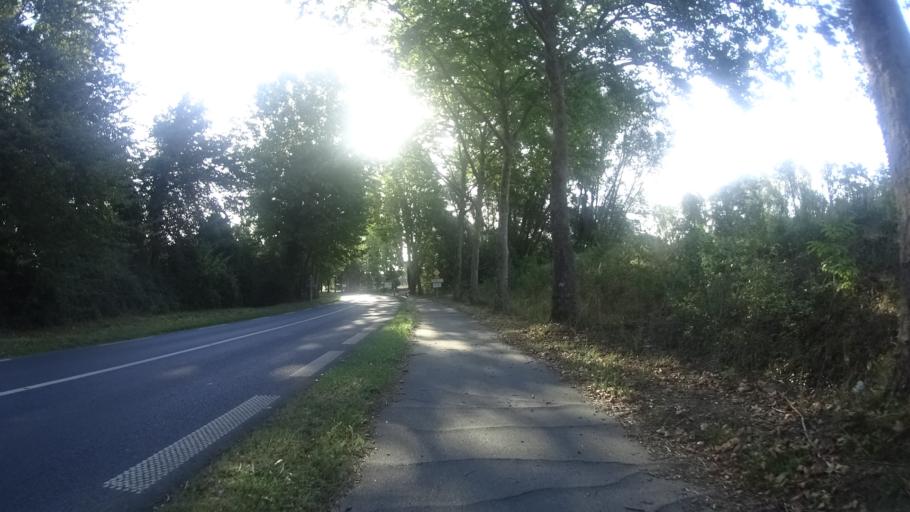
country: FR
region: Picardie
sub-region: Departement de l'Oise
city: Verberie
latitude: 49.3068
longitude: 2.7156
